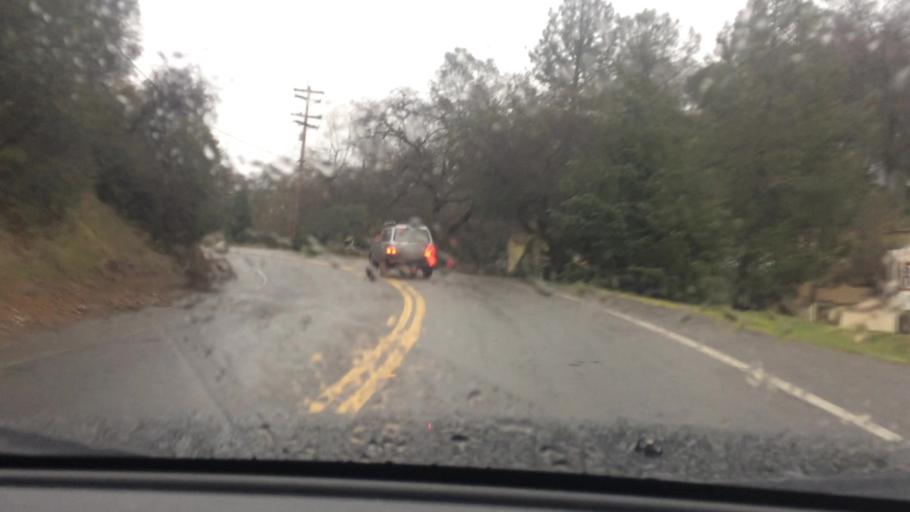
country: US
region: California
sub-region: El Dorado County
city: Deer Park
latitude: 38.6816
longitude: -120.8431
